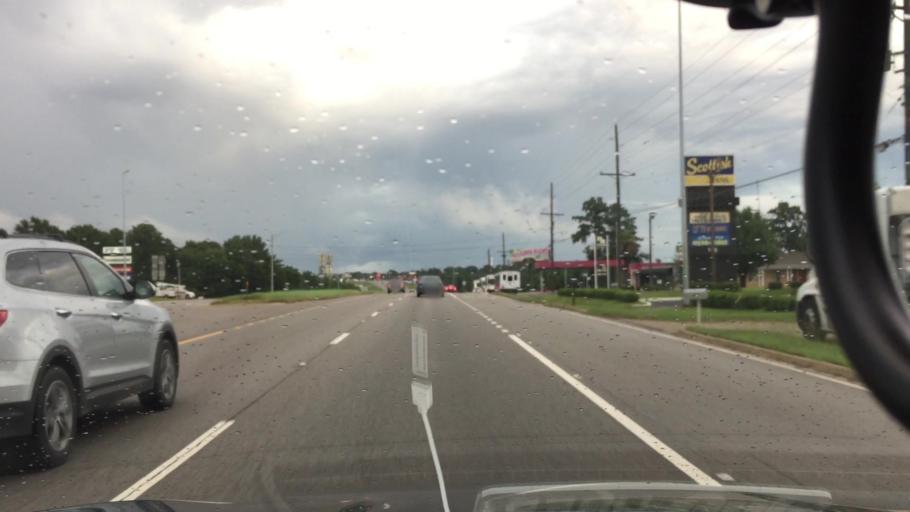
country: US
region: Alabama
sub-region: Pike County
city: Troy
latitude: 31.8041
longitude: -85.9870
